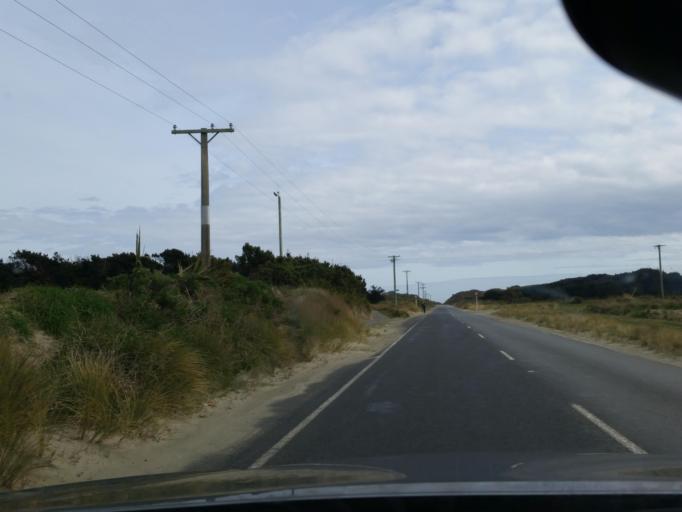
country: NZ
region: Southland
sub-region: Invercargill City
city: Invercargill
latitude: -46.4375
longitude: 168.2404
